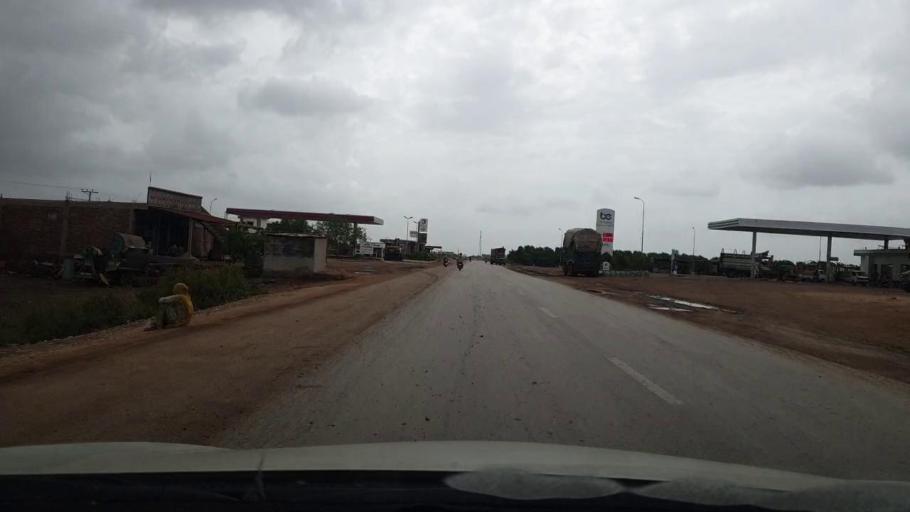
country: PK
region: Sindh
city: Mirpur Batoro
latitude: 24.6185
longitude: 68.2970
